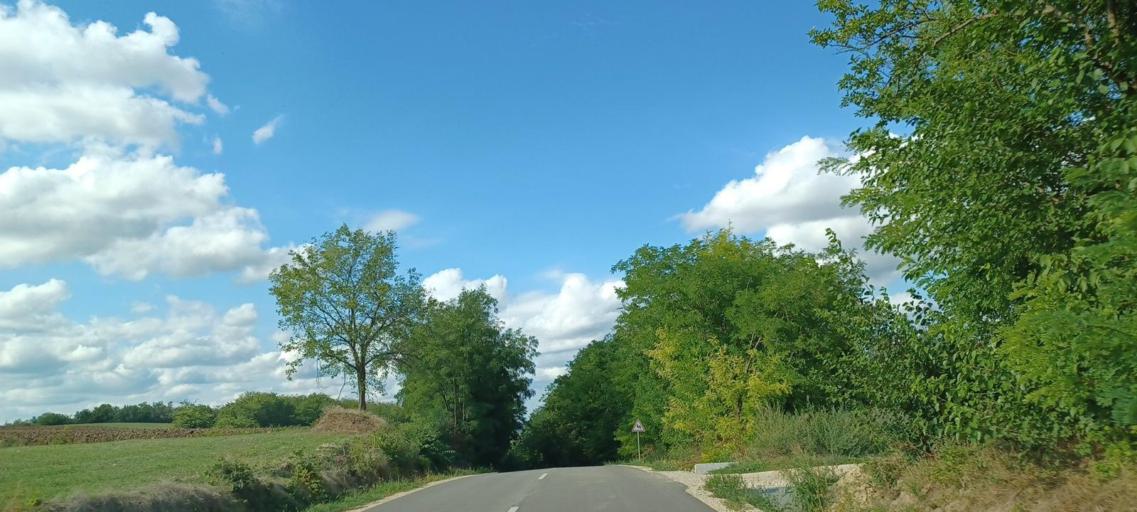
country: HU
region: Tolna
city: Zomba
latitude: 46.4928
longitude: 18.5930
